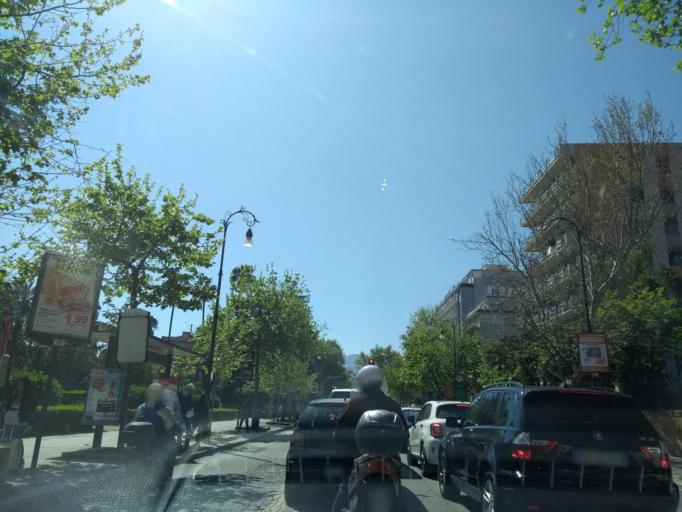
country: IT
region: Sicily
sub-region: Palermo
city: Palermo
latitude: 38.1344
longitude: 13.3494
